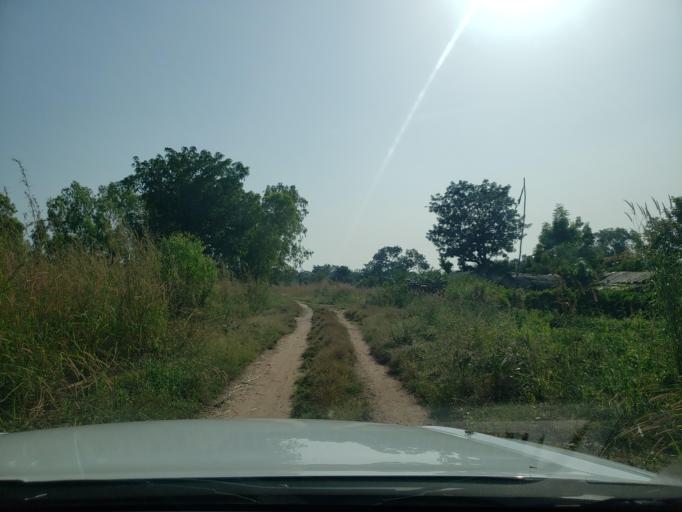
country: TG
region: Kara
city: Bafilo
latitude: 9.4105
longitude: 1.1802
